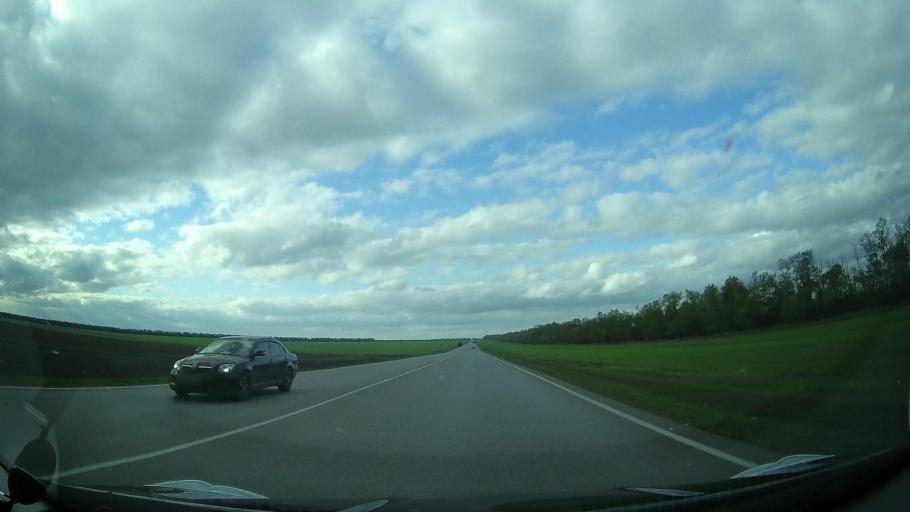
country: RU
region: Rostov
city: Kagal'nitskaya
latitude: 46.9025
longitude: 40.1214
